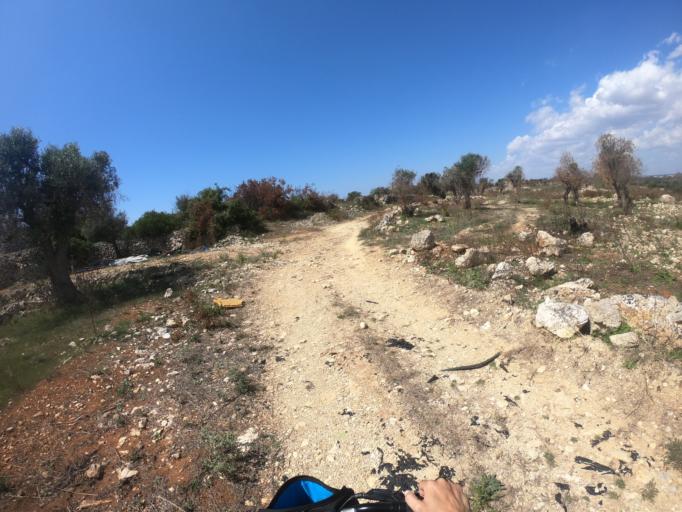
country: IT
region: Apulia
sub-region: Provincia di Lecce
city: Secli
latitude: 40.1197
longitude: 18.0819
